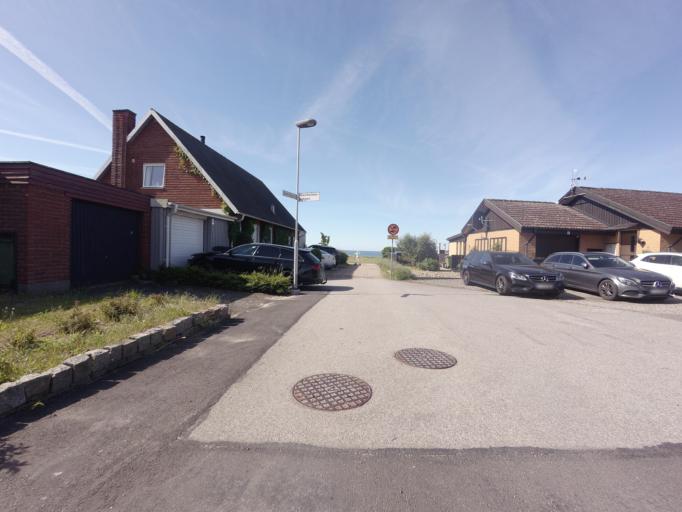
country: SE
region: Skane
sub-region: Trelleborgs Kommun
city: Skare
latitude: 55.3770
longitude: 13.0491
